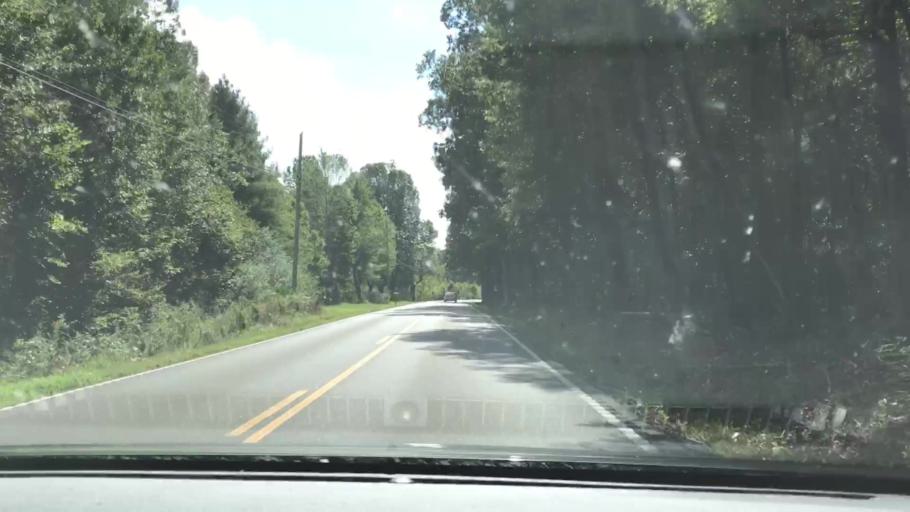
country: US
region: Kentucky
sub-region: McCracken County
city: Reidland
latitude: 36.9650
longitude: -88.5141
